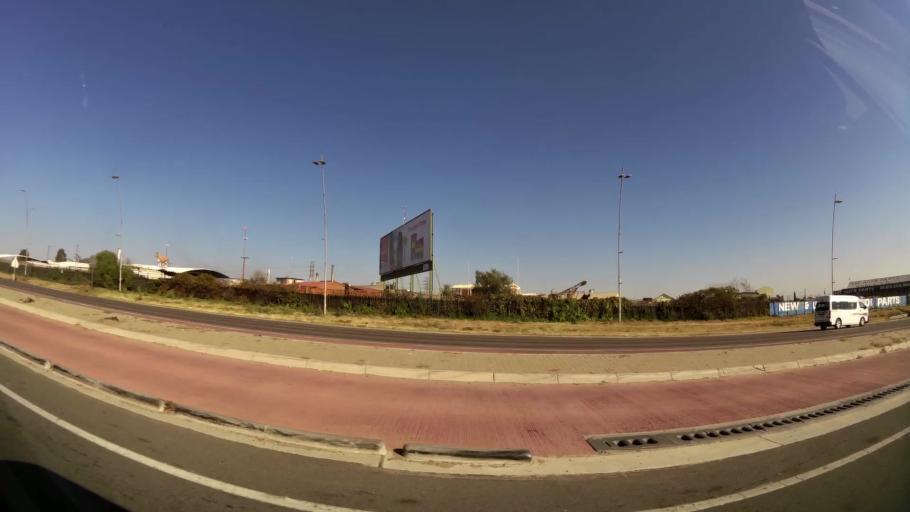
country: ZA
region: Gauteng
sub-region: City of Johannesburg Metropolitan Municipality
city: Modderfontein
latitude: -26.0674
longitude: 28.1859
